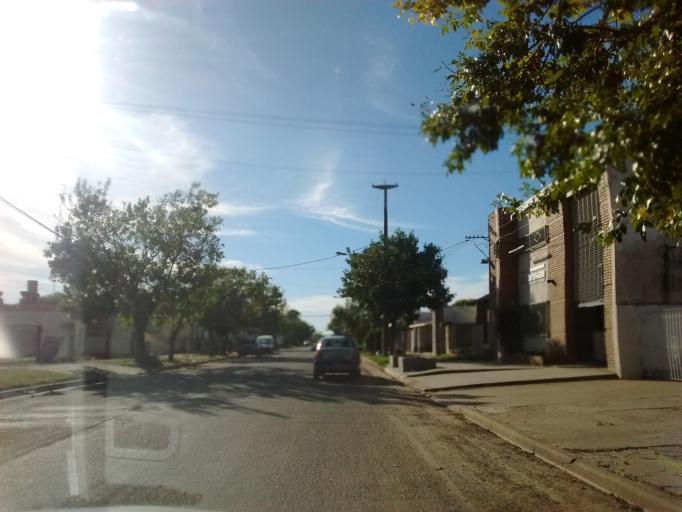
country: AR
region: Santa Fe
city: Coronda
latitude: -32.2311
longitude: -60.9841
